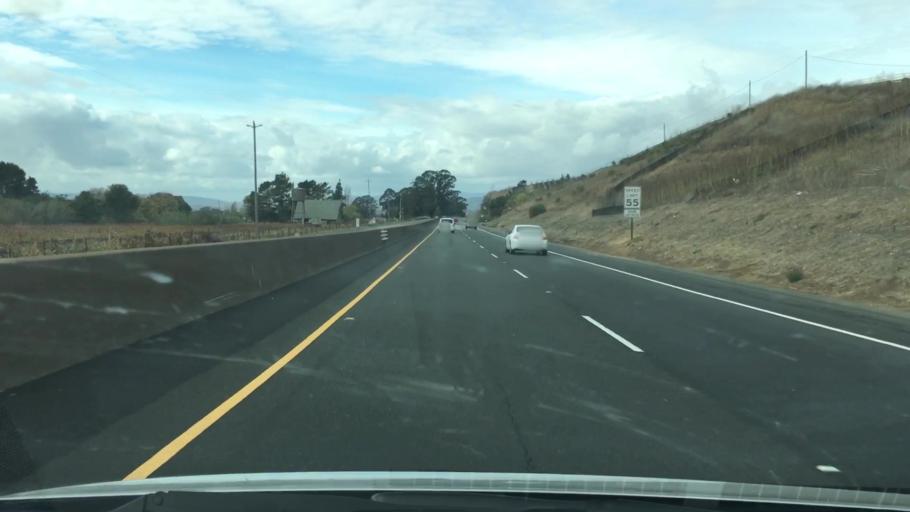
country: US
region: California
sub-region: Napa County
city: American Canyon
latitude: 38.2136
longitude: -122.2144
